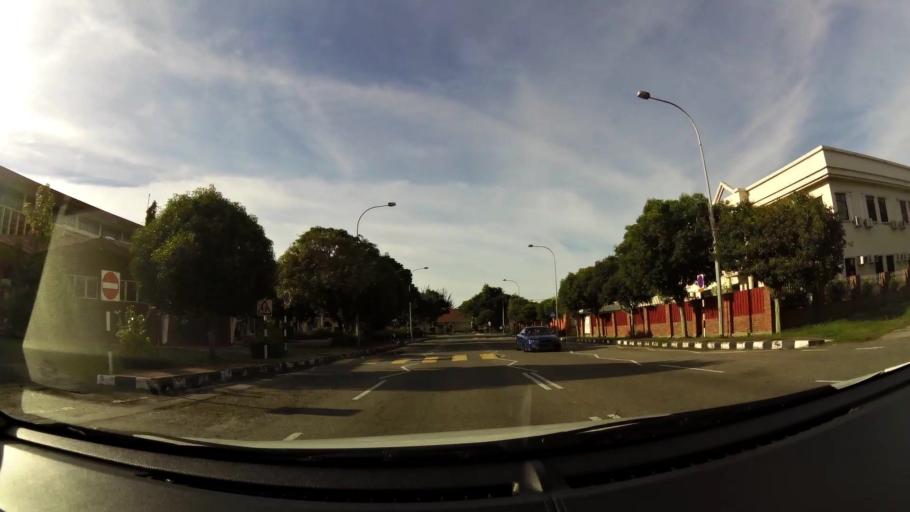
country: BN
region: Belait
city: Kuala Belait
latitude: 4.5876
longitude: 114.1932
